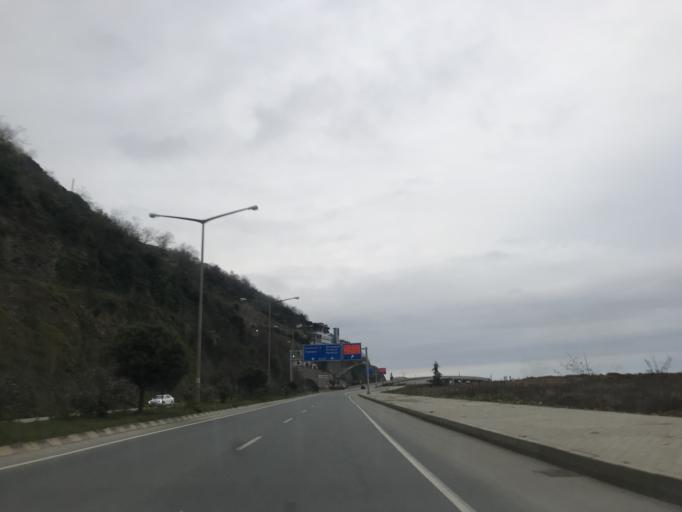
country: TR
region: Trabzon
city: Derecik
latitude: 40.9990
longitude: 39.6402
